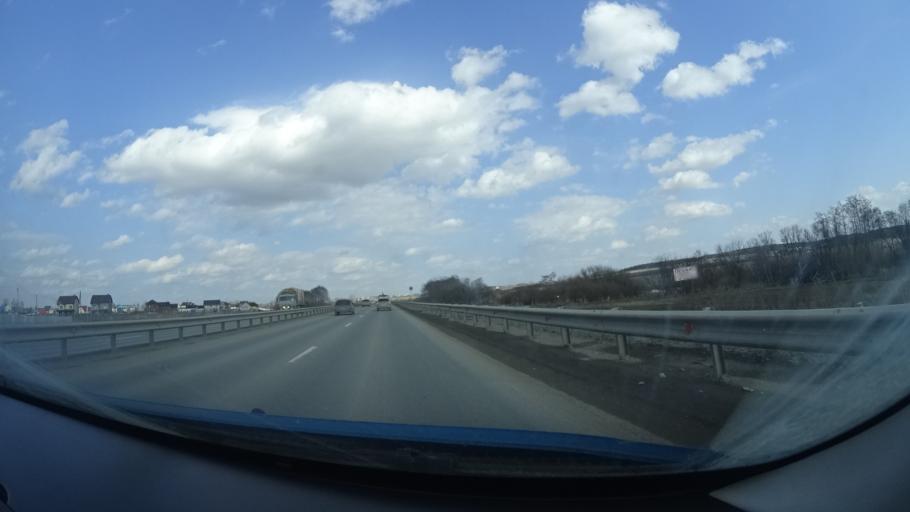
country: RU
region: Perm
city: Kultayevo
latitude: 57.8997
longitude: 55.9721
